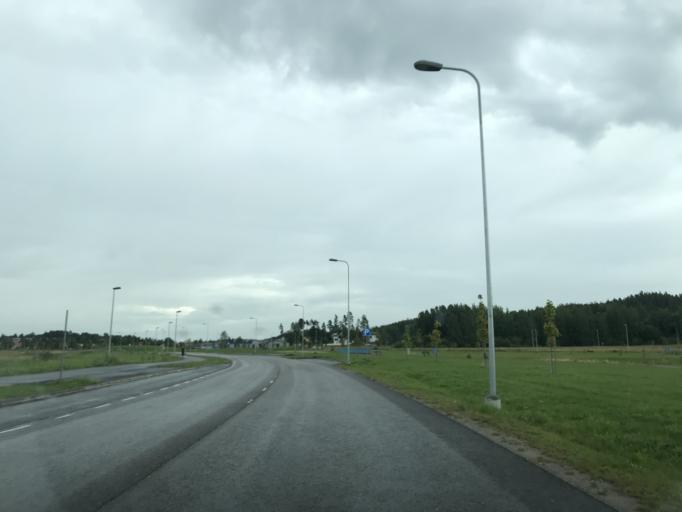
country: FI
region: Uusimaa
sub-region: Helsinki
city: Vihti
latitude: 60.3200
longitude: 24.3123
